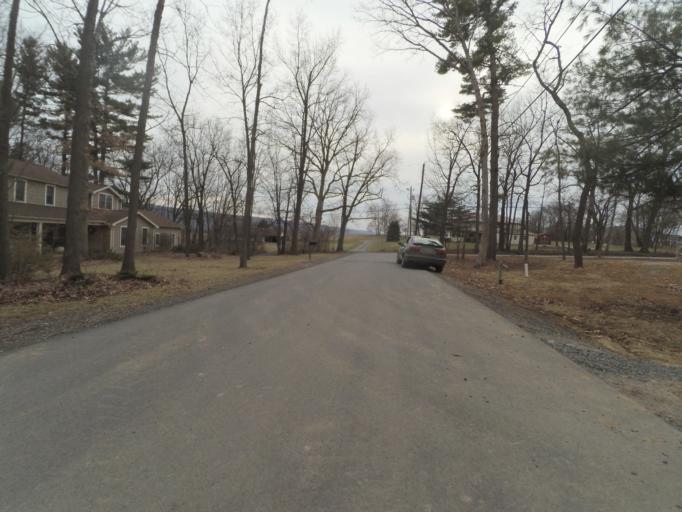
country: US
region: Pennsylvania
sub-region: Centre County
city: State College
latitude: 40.7724
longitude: -77.8502
